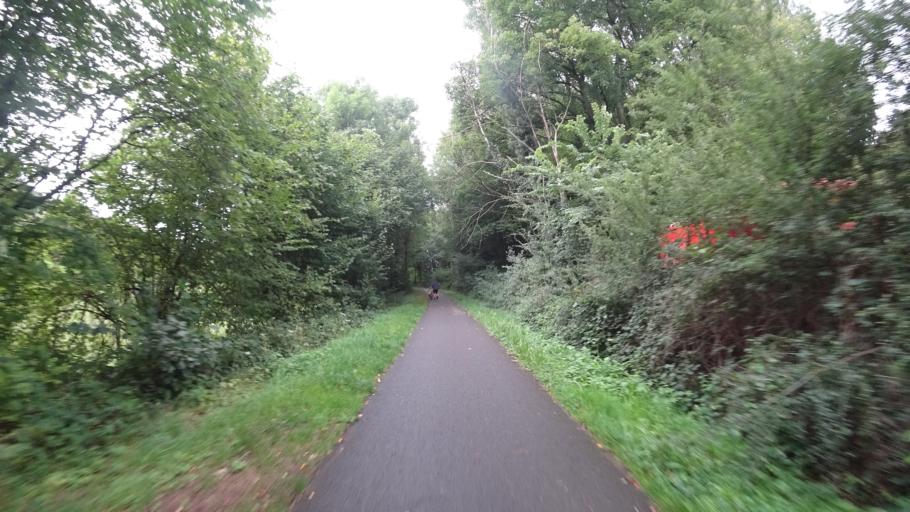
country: BE
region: Wallonia
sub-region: Province de Namur
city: Namur
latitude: 50.4986
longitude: 4.8671
